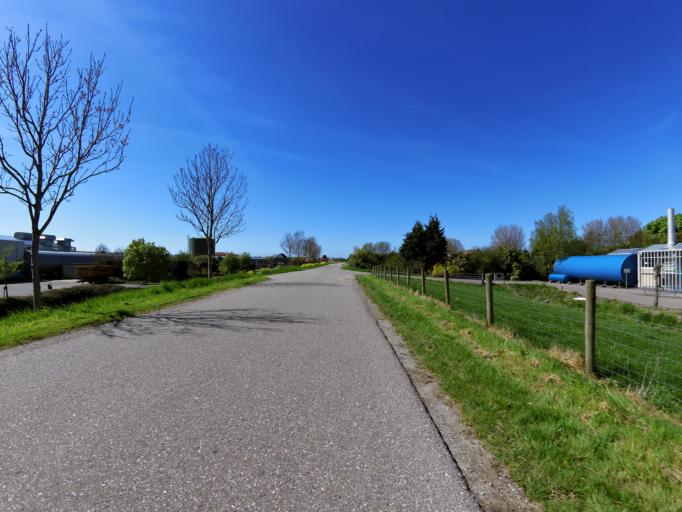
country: NL
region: South Holland
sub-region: Gemeente Brielle
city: Brielle
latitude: 51.8980
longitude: 4.1272
